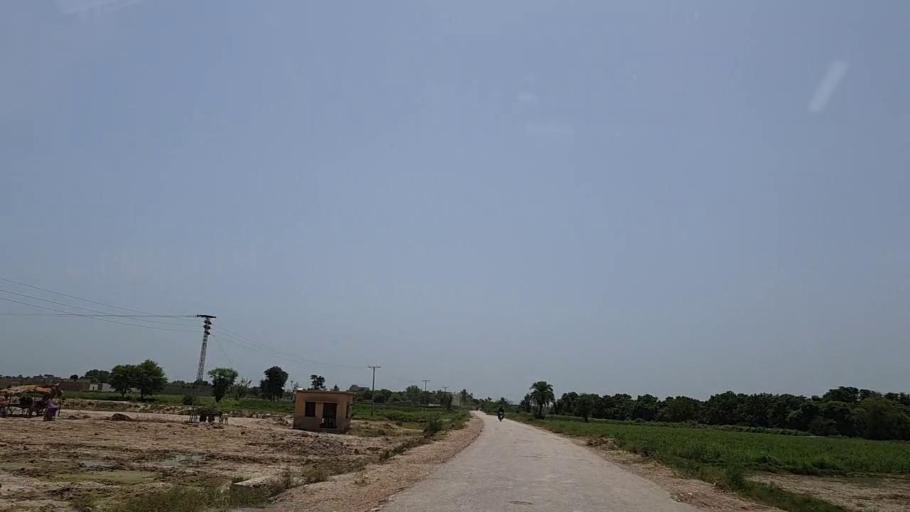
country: PK
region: Sindh
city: Tharu Shah
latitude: 26.9442
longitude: 68.1067
